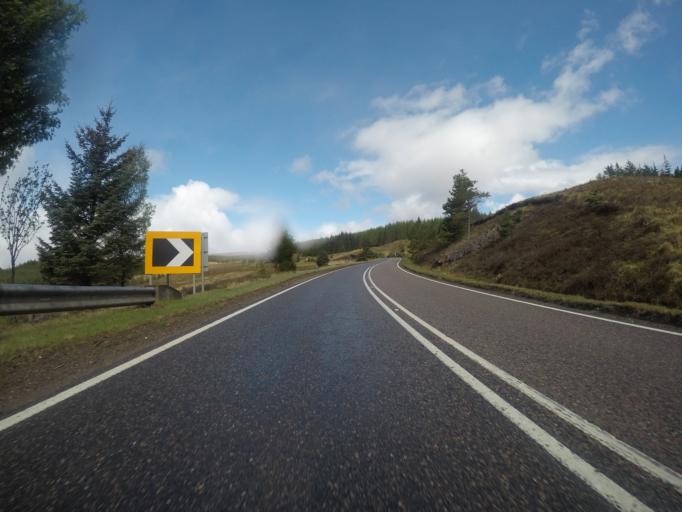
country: GB
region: Scotland
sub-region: Highland
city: Spean Bridge
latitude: 57.0885
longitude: -4.9811
